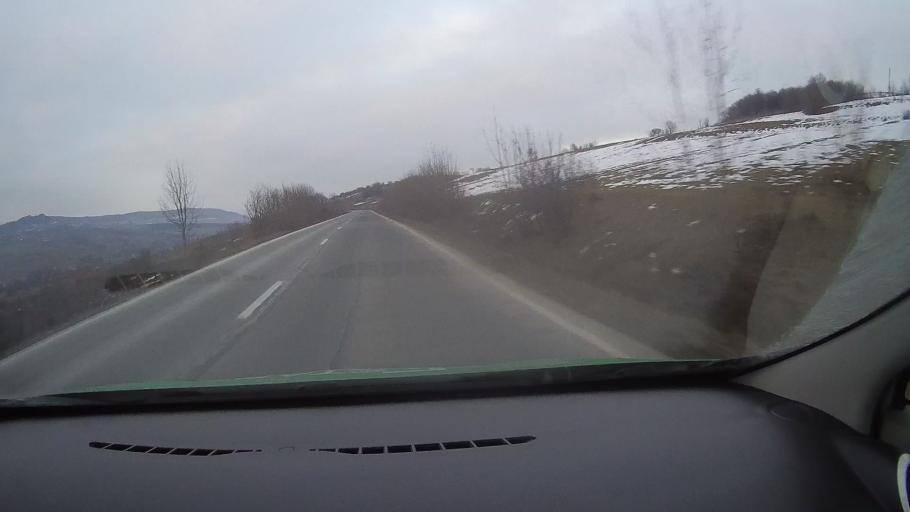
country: RO
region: Harghita
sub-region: Comuna Lupeni
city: Lupeni
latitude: 46.3564
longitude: 25.2439
